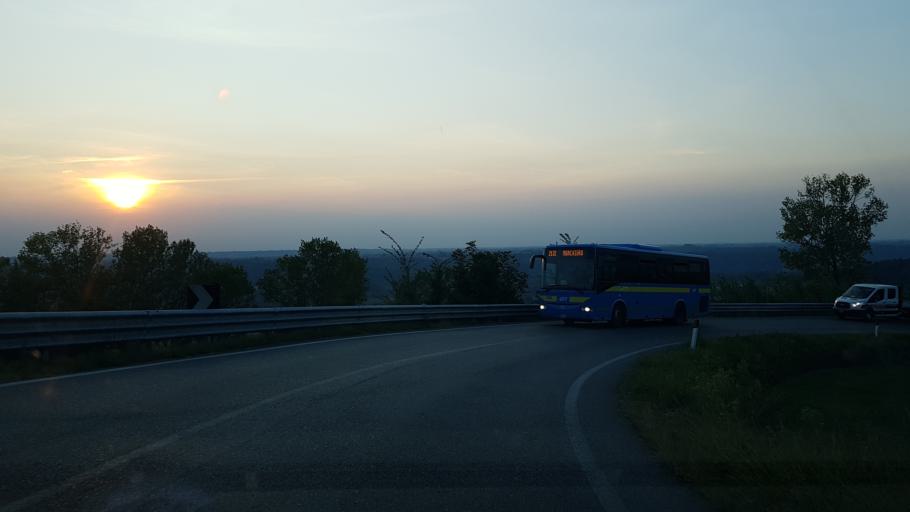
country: IT
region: Piedmont
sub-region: Provincia di Cuneo
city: Novello
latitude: 44.5830
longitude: 7.9146
